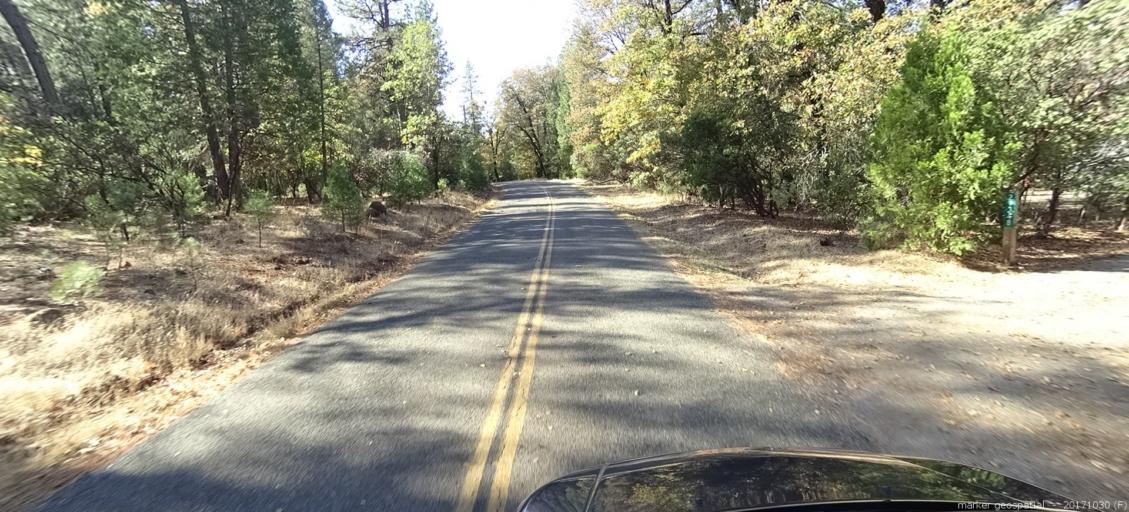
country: US
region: California
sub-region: Shasta County
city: Shingletown
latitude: 40.6037
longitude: -121.9569
